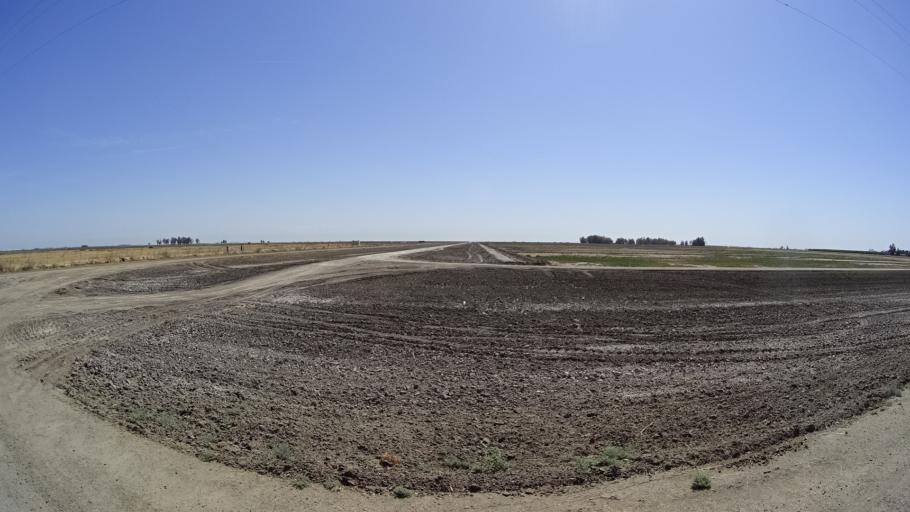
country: US
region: California
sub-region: Kings County
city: Stratford
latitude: 36.1743
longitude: -119.7803
